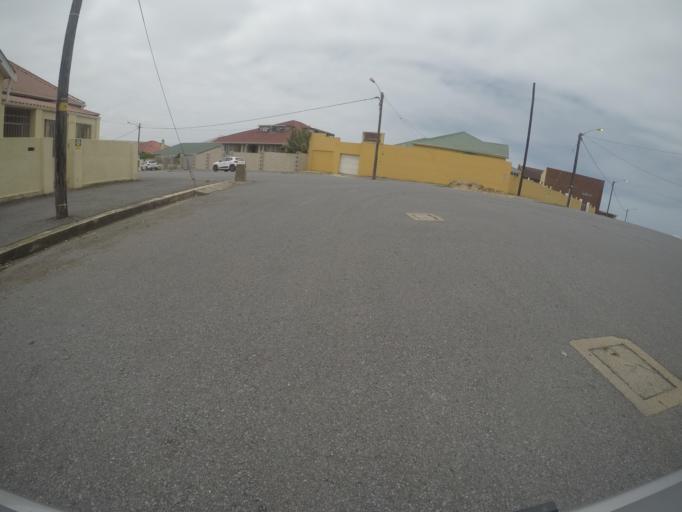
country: ZA
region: Eastern Cape
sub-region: Buffalo City Metropolitan Municipality
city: East London
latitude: -33.0158
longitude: 27.9173
